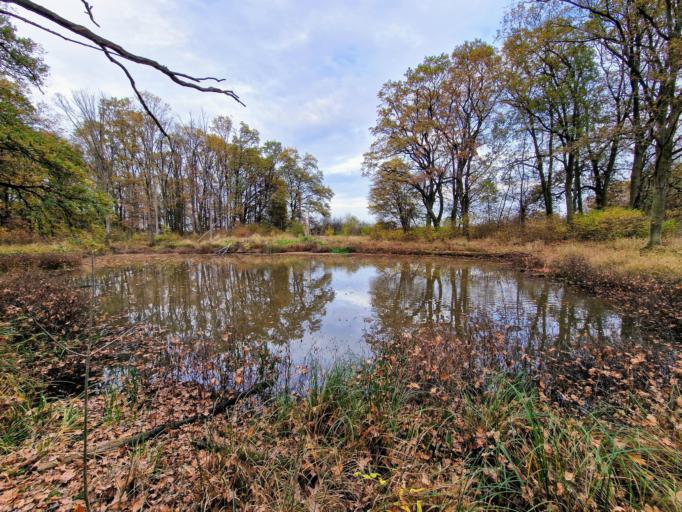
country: PL
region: Lubusz
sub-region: Powiat zielonogorski
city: Klenica
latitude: 51.9663
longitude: 15.7730
